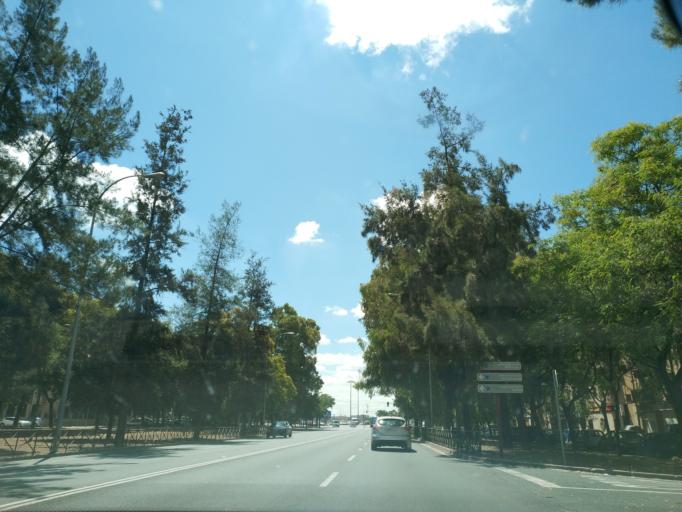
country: ES
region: Andalusia
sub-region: Provincia de Sevilla
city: Sevilla
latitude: 37.3624
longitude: -5.9608
